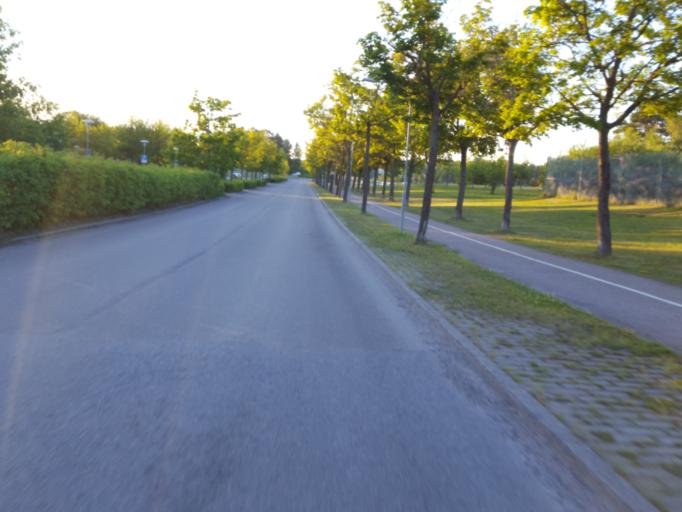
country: SE
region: Uppsala
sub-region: Uppsala Kommun
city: Saevja
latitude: 59.8195
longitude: 17.6572
